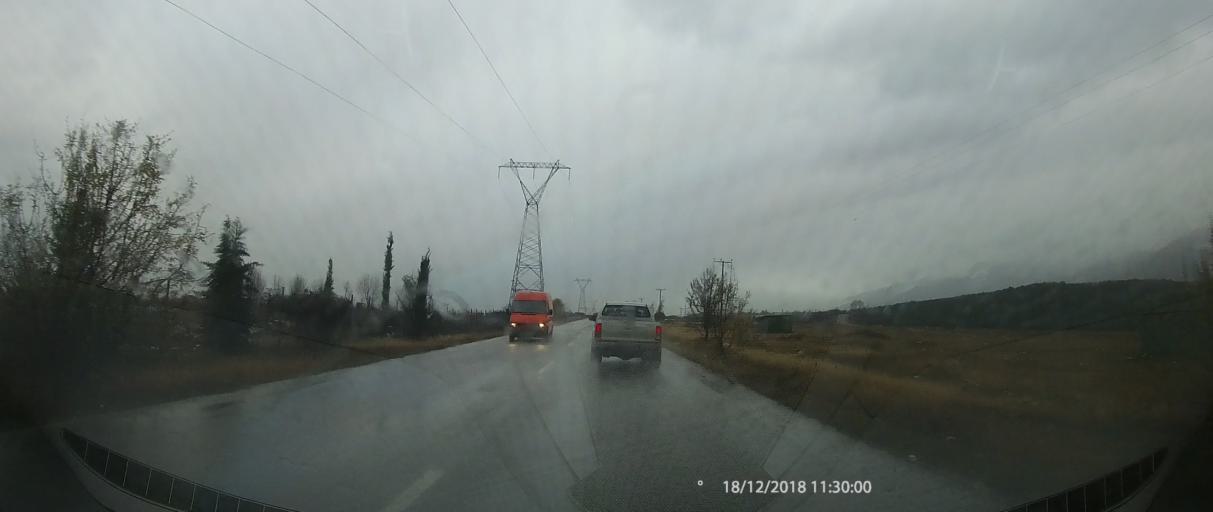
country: GR
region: Central Macedonia
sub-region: Nomos Pierias
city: Litochoro
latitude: 40.1286
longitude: 22.5223
